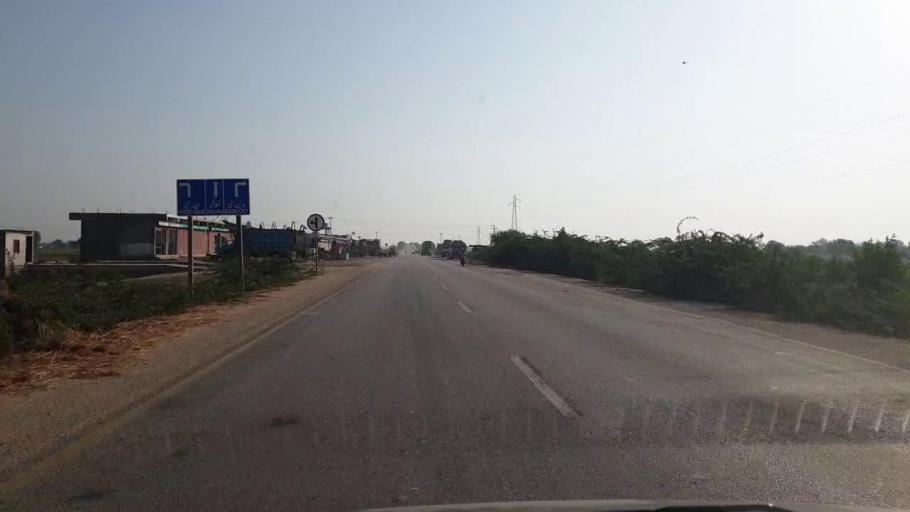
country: PK
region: Sindh
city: Badin
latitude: 24.6793
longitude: 68.8235
